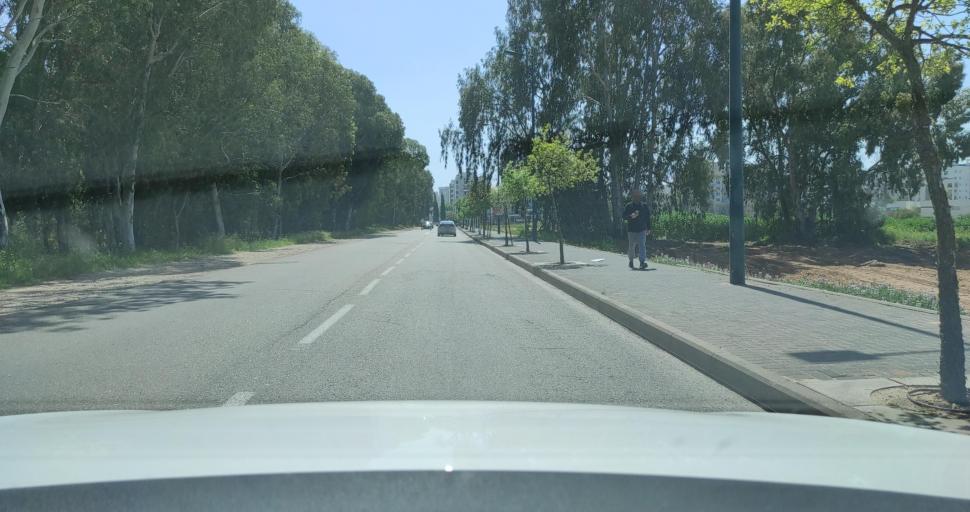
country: IL
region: Central District
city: Nordiyya
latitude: 32.3058
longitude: 34.8742
